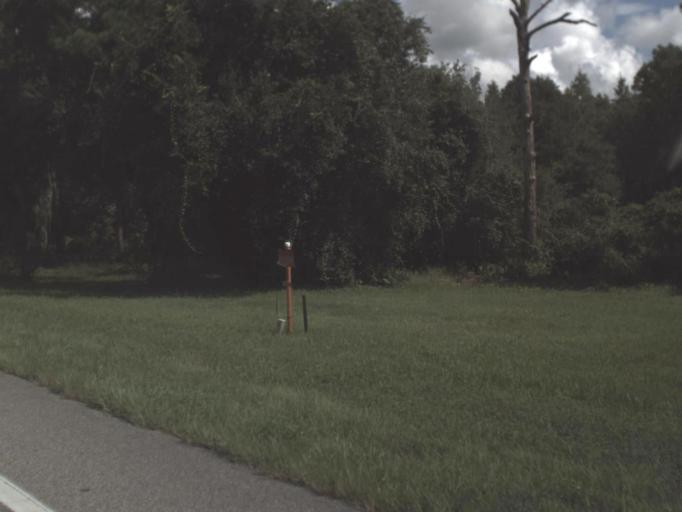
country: US
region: Florida
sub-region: Polk County
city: Polk City
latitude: 28.2643
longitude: -81.8268
